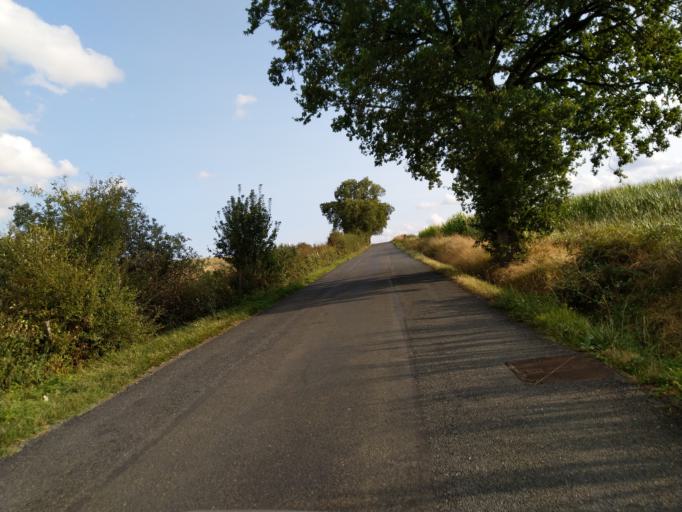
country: FR
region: Midi-Pyrenees
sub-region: Departement du Tarn
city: Frejairolles
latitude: 43.8715
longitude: 2.2336
